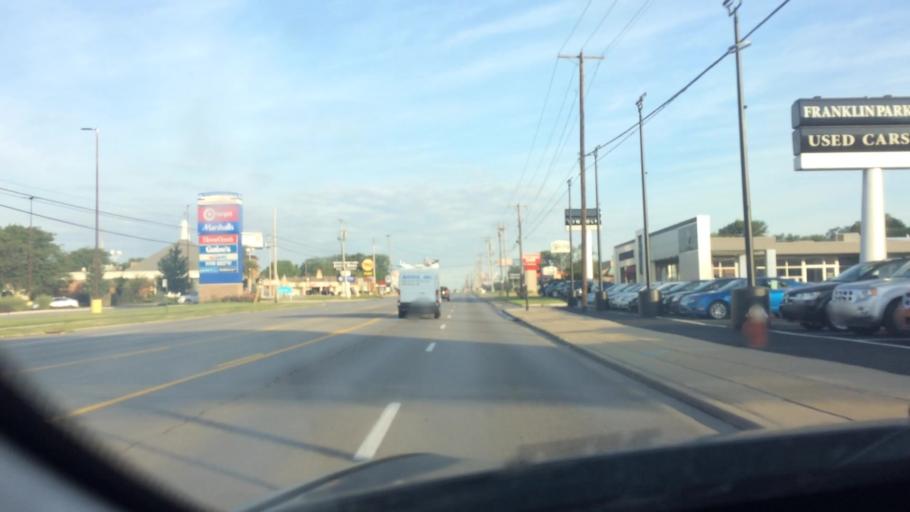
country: US
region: Ohio
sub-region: Lucas County
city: Ottawa Hills
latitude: 41.7020
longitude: -83.6530
